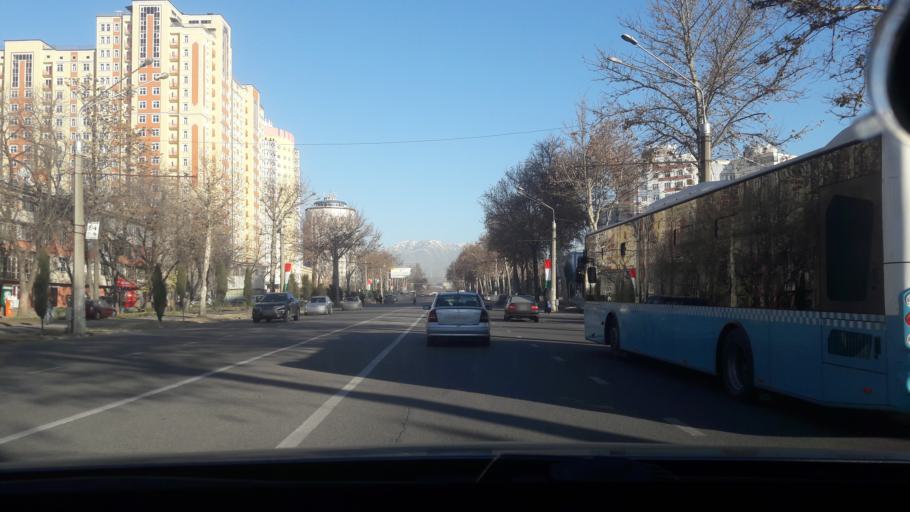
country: TJ
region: Dushanbe
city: Dushanbe
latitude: 38.5603
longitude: 68.7550
